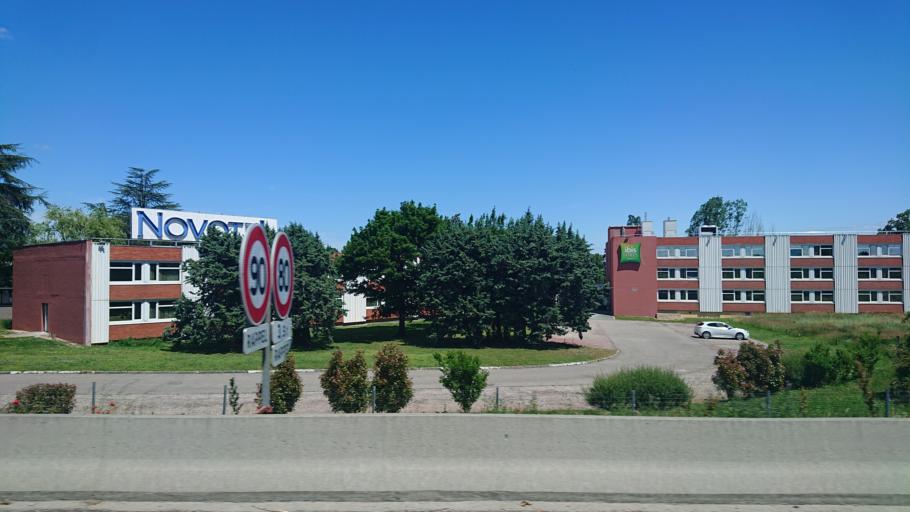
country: FR
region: Rhone-Alpes
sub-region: Departement du Rhone
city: Bron
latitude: 45.7236
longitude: 4.9284
